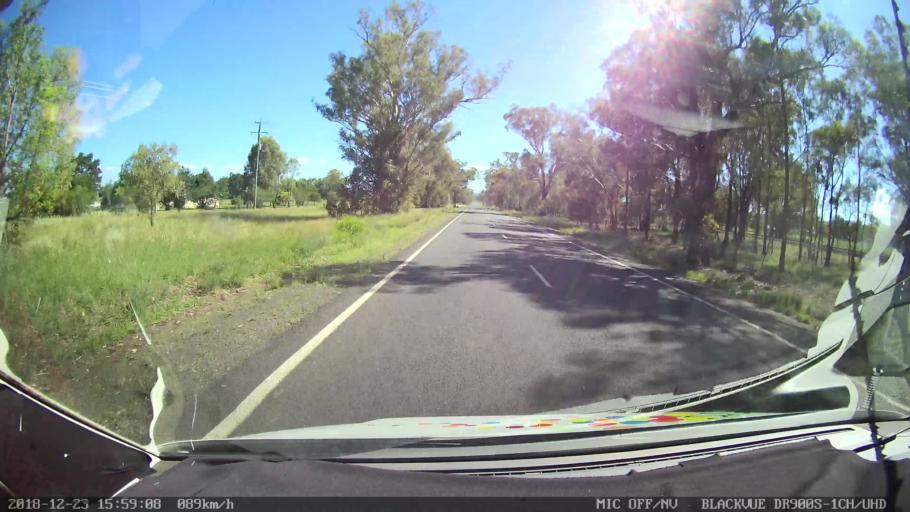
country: AU
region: New South Wales
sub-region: Tamworth Municipality
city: Phillip
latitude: -31.1962
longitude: 150.8358
